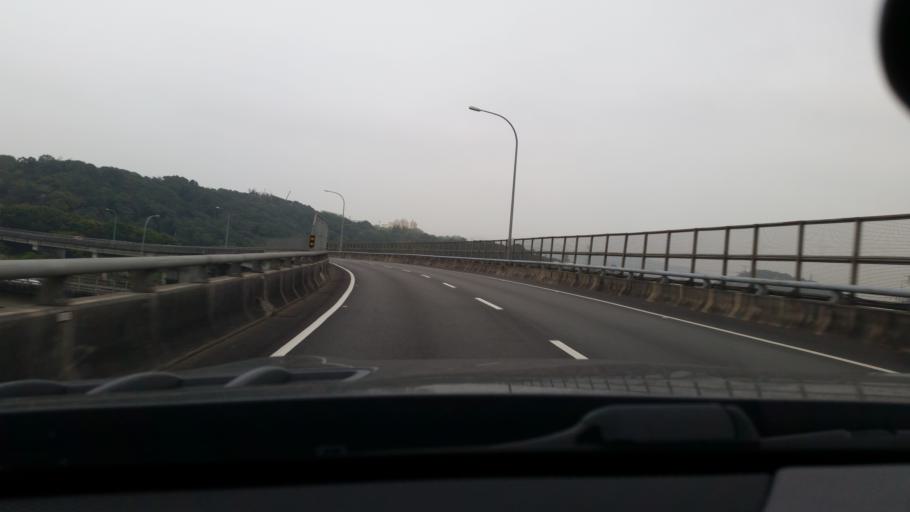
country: TW
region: Taiwan
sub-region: Taoyuan
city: Taoyuan
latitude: 24.9388
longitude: 121.3245
